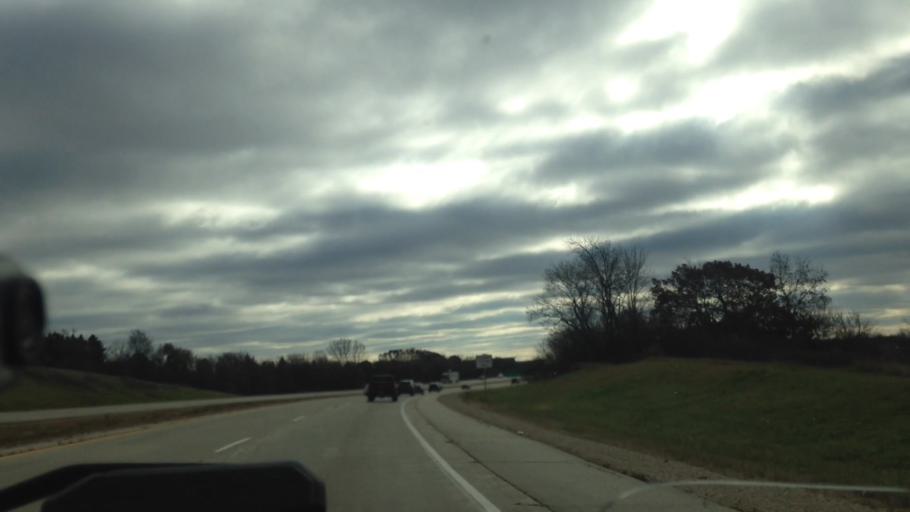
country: US
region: Wisconsin
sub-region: Washington County
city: West Bend
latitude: 43.4051
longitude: -88.1968
